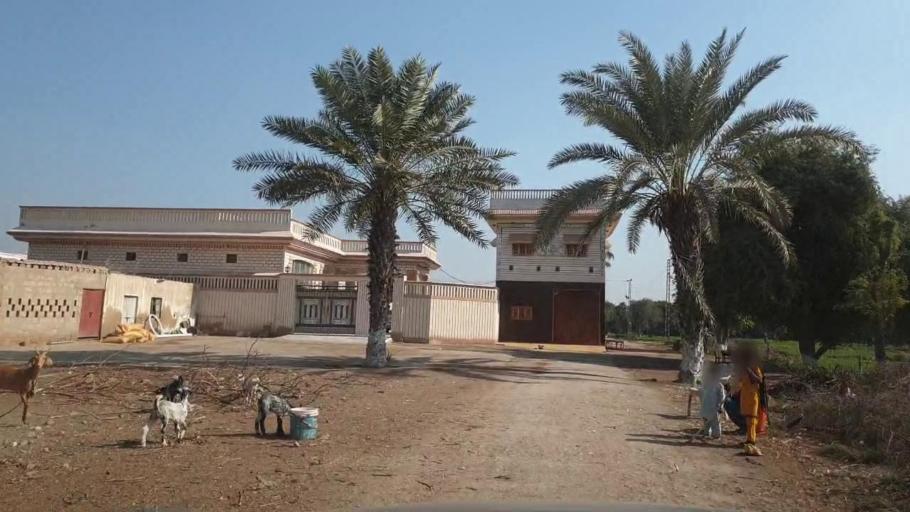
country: PK
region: Sindh
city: Tando Allahyar
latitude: 25.5806
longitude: 68.7459
